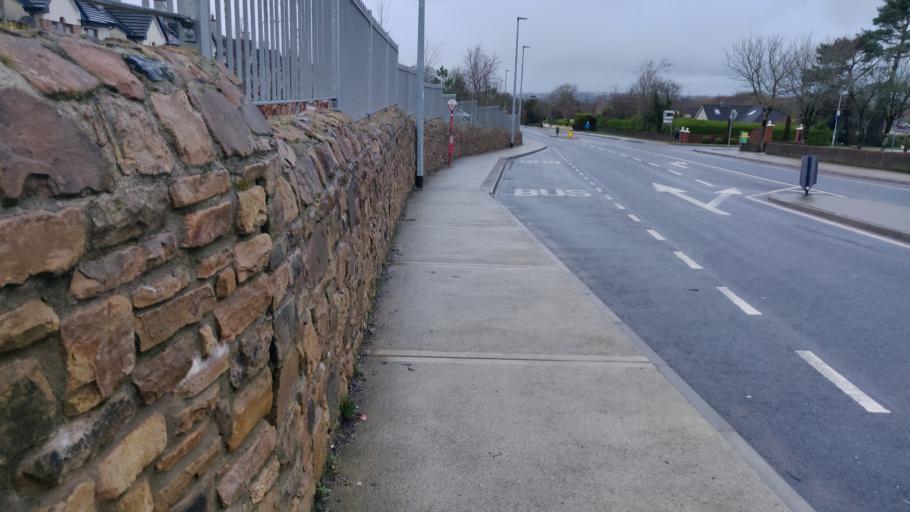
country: IE
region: Munster
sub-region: County Cork
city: Carrigaline
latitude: 51.8638
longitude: -8.4129
